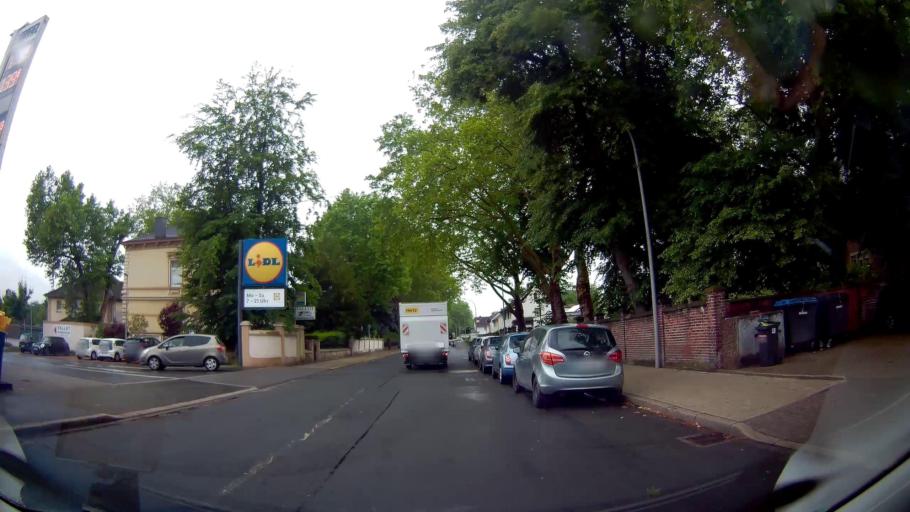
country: DE
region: North Rhine-Westphalia
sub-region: Regierungsbezirk Munster
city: Gelsenkirchen
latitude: 51.4938
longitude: 7.1435
